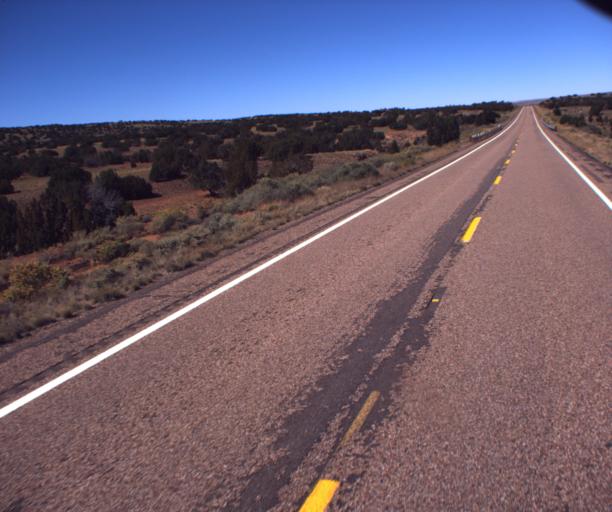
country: US
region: Arizona
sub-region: Apache County
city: Saint Johns
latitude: 34.5753
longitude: -109.5298
